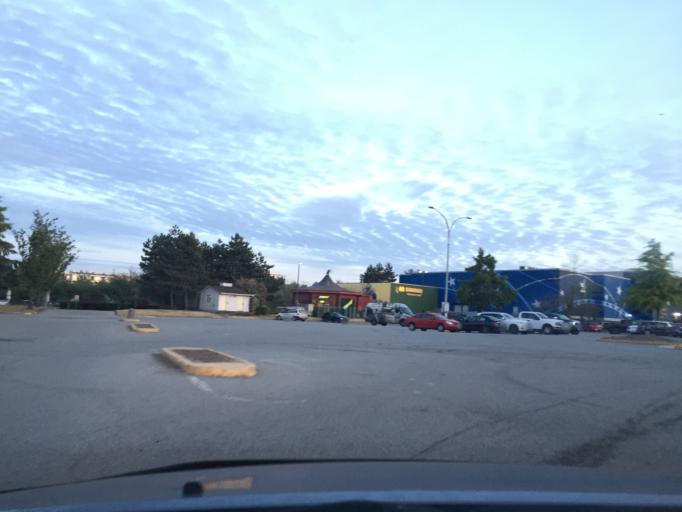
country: CA
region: British Columbia
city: Ladner
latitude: 49.1366
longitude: -123.0651
